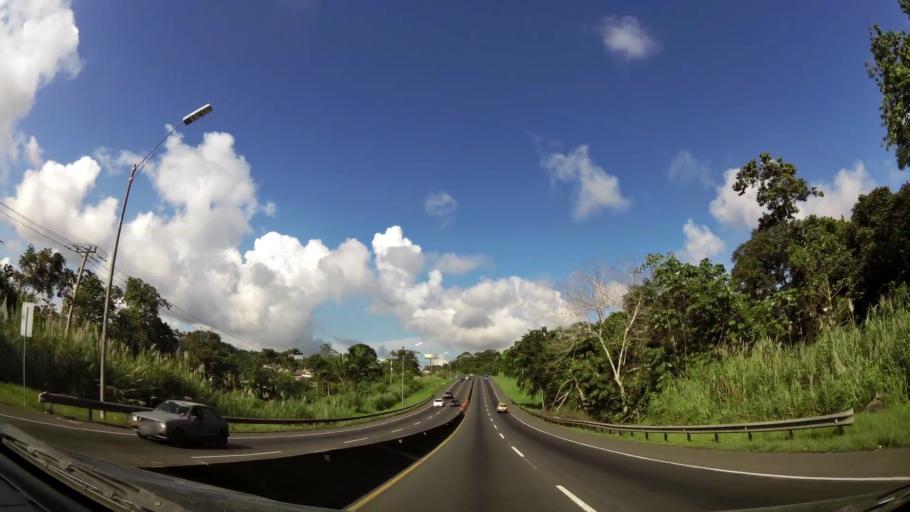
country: PA
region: Panama
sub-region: Distrito Arraijan
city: Arraijan
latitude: 8.9549
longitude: -79.6441
